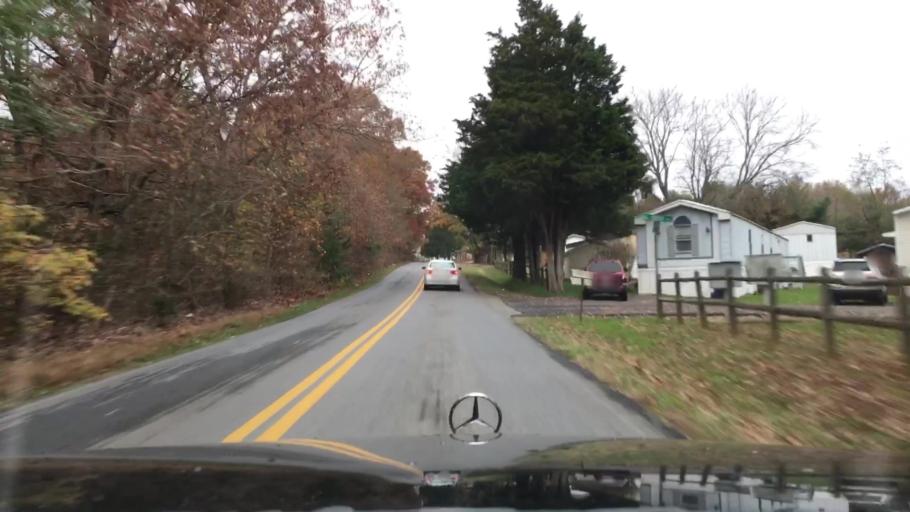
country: US
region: Virginia
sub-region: Campbell County
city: Timberlake
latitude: 37.2944
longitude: -79.2803
